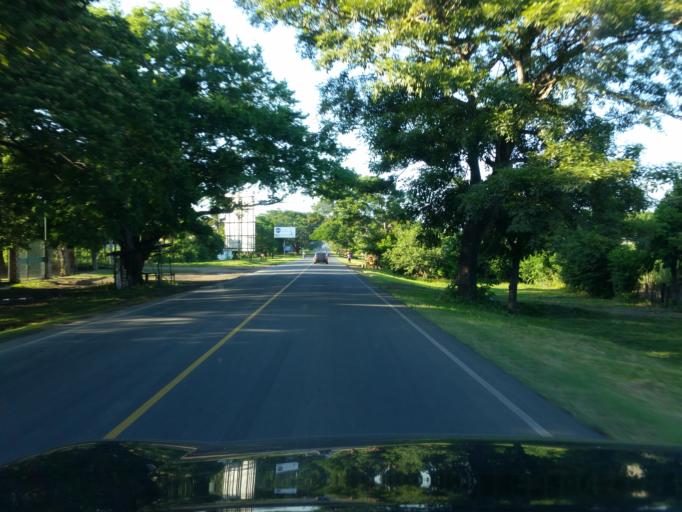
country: NI
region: Rivas
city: Potosi
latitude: 11.4782
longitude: -85.8651
